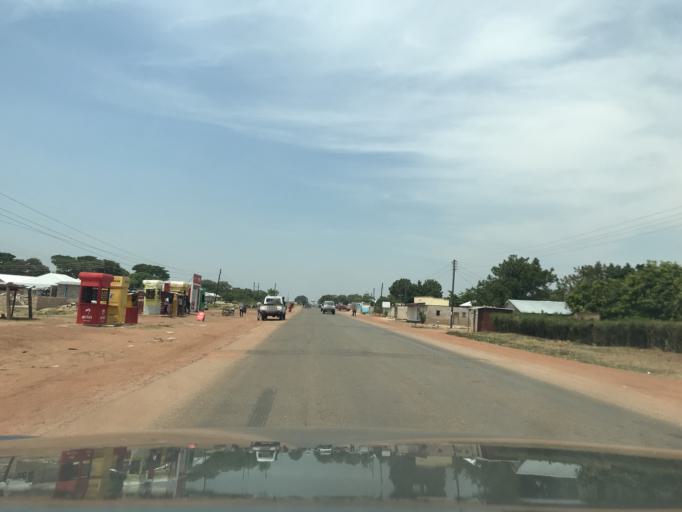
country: ZM
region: Northern
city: Kasama
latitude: -10.2143
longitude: 31.1535
